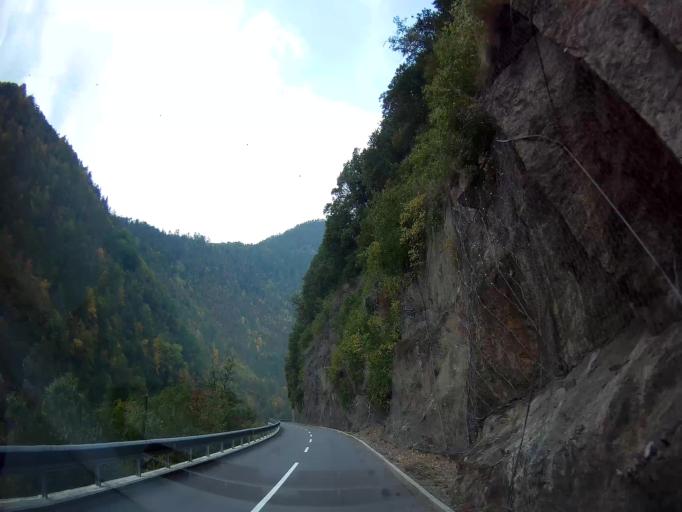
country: IT
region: Trentino-Alto Adige
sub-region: Bolzano
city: Naturno
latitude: 46.6565
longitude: 10.9640
